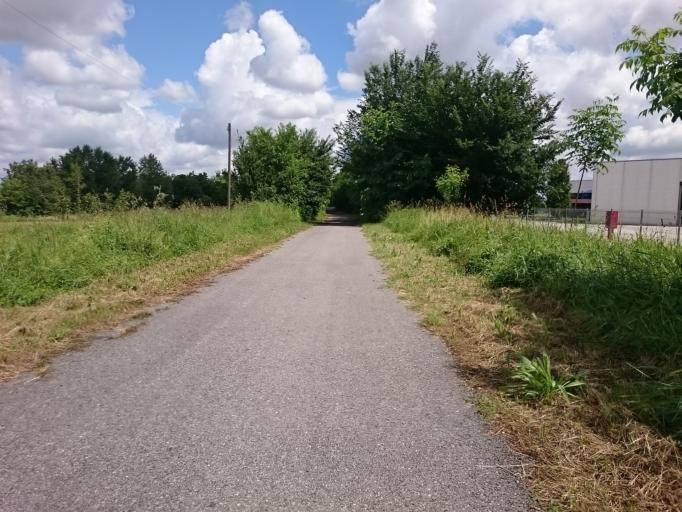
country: IT
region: Veneto
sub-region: Provincia di Padova
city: Campodoro
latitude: 45.5034
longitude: 11.7446
